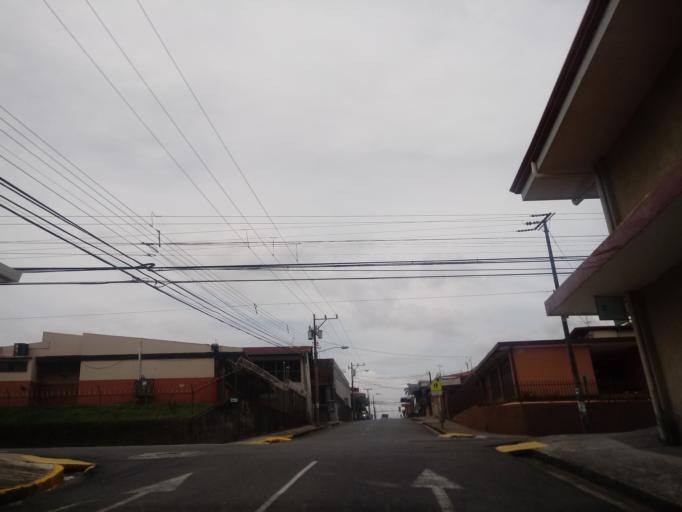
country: CR
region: Heredia
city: Heredia
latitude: 10.0015
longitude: -84.1178
